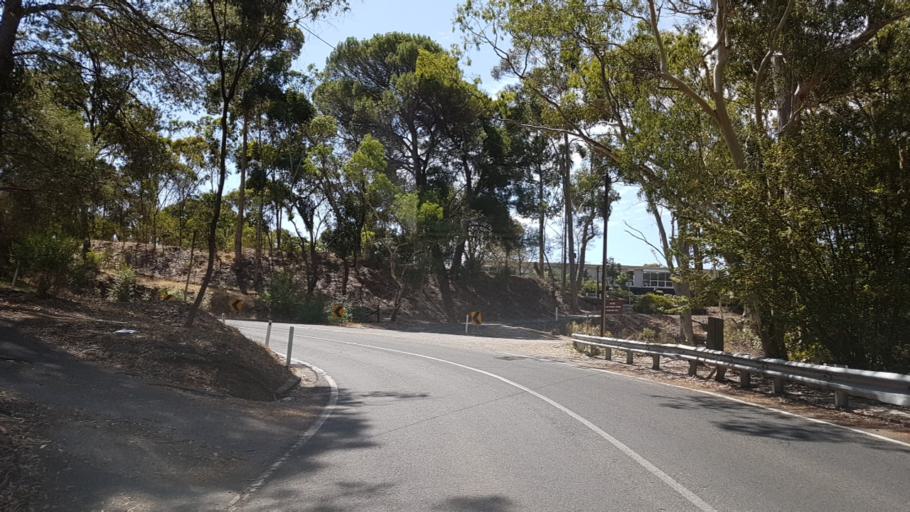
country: AU
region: South Australia
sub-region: Mitcham
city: Belair
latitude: -34.9990
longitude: 138.6325
